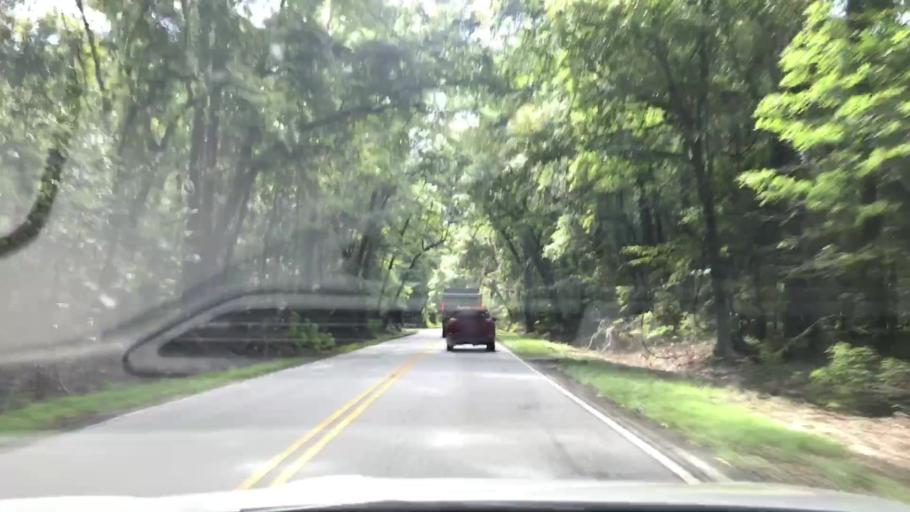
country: US
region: South Carolina
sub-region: Berkeley County
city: Ladson
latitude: 32.8957
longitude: -80.1357
